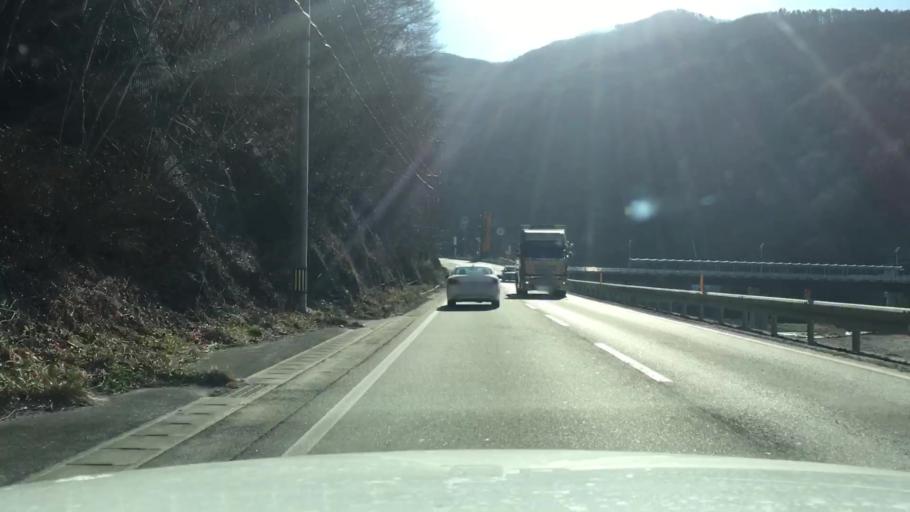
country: JP
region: Iwate
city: Miyako
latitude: 39.6173
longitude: 141.7955
